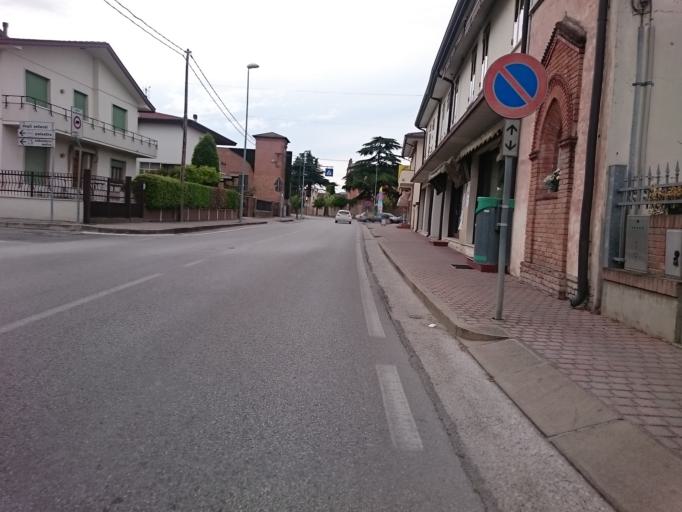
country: IT
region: Veneto
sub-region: Provincia di Padova
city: Sant'Elena
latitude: 45.1881
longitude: 11.7111
